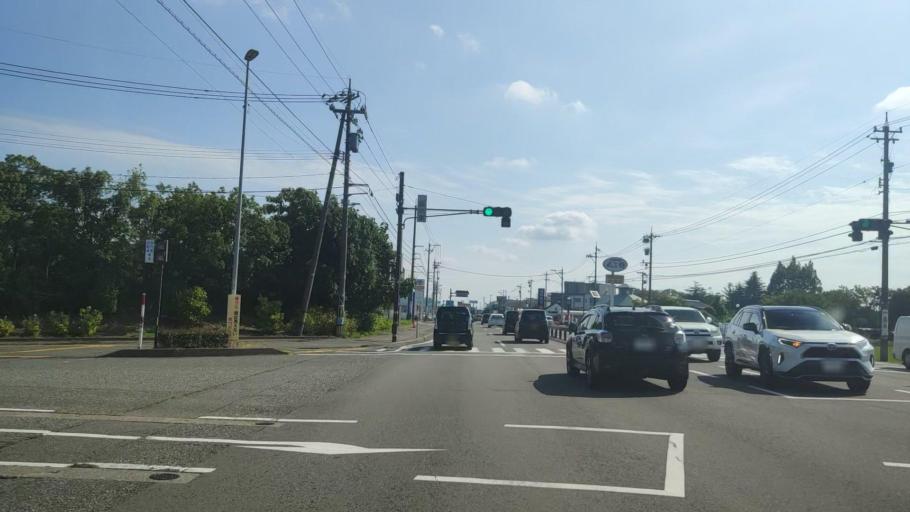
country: JP
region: Ishikawa
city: Matsuto
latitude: 36.5138
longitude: 136.5725
